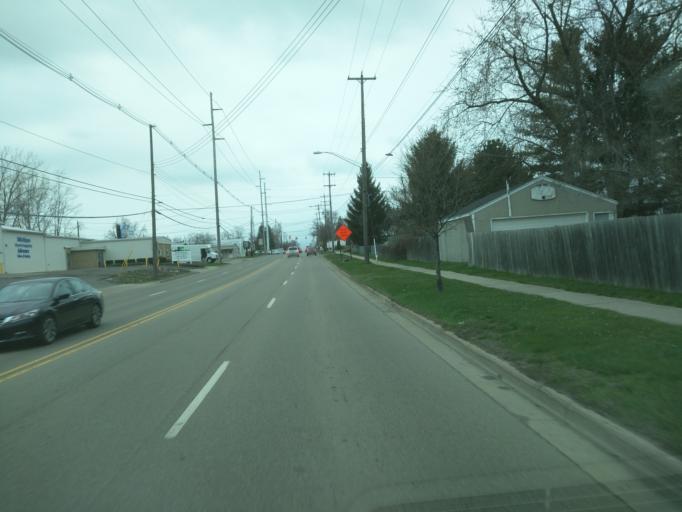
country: US
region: Michigan
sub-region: Ingham County
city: Holt
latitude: 42.6830
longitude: -84.5356
